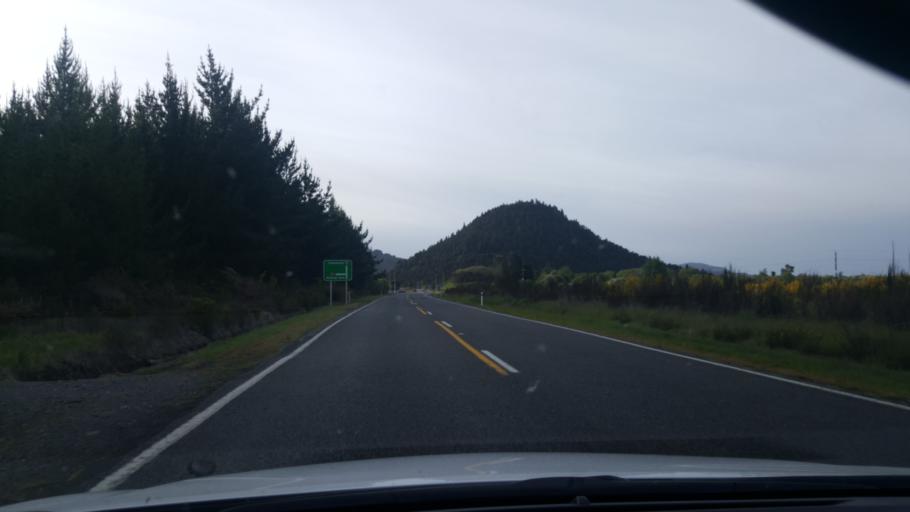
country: NZ
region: Waikato
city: Turangi
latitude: -38.9836
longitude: 175.7822
